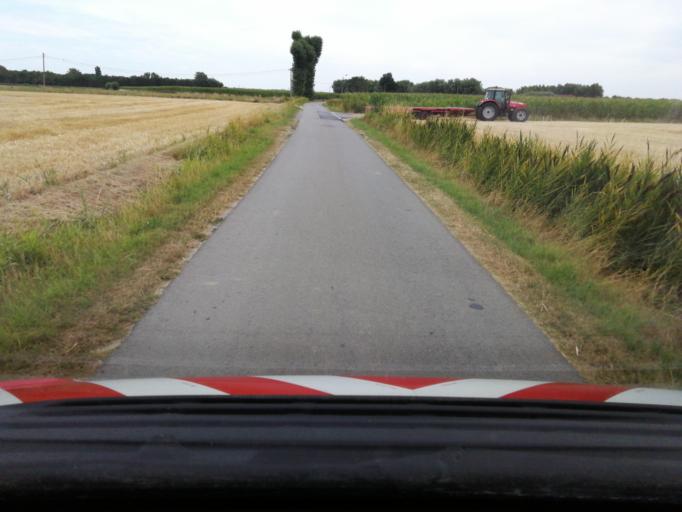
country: BE
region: Flanders
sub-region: Provincie West-Vlaanderen
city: Knokke-Heist
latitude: 51.3148
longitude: 3.2571
